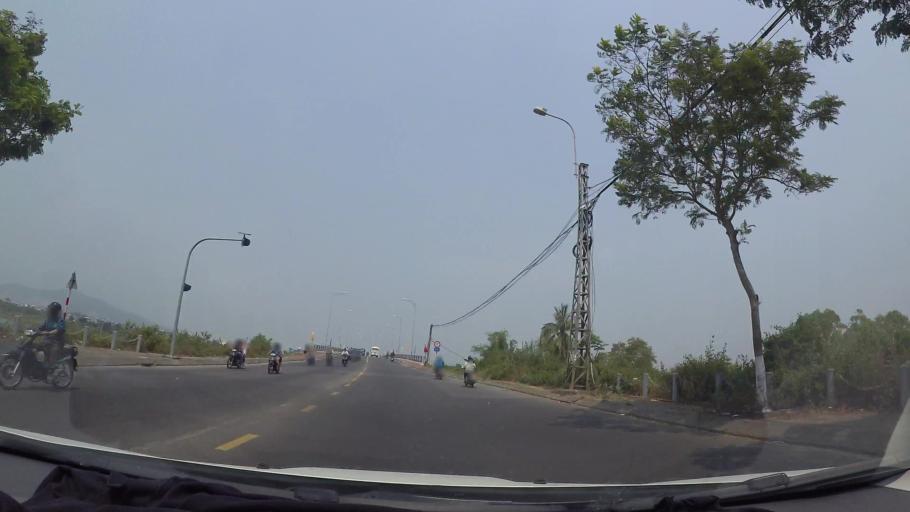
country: VN
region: Da Nang
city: Cam Le
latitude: 16.0072
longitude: 108.2077
